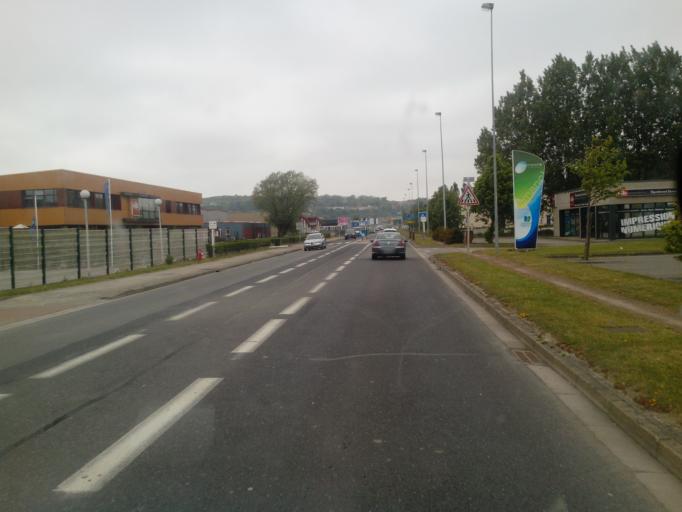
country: FR
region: Nord-Pas-de-Calais
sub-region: Departement du Pas-de-Calais
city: Saint-Leonard
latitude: 50.6898
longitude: 1.6176
